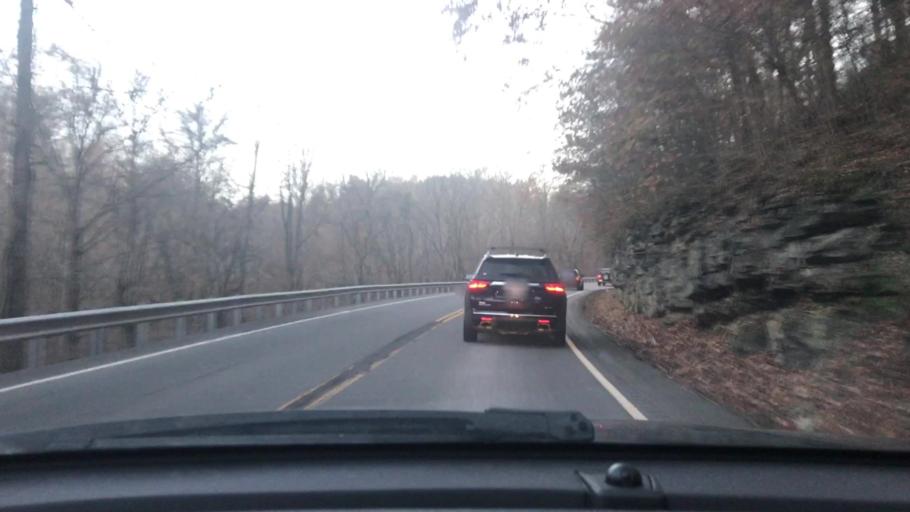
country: US
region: Tennessee
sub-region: Cheatham County
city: Ashland City
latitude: 36.3084
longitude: -87.0442
